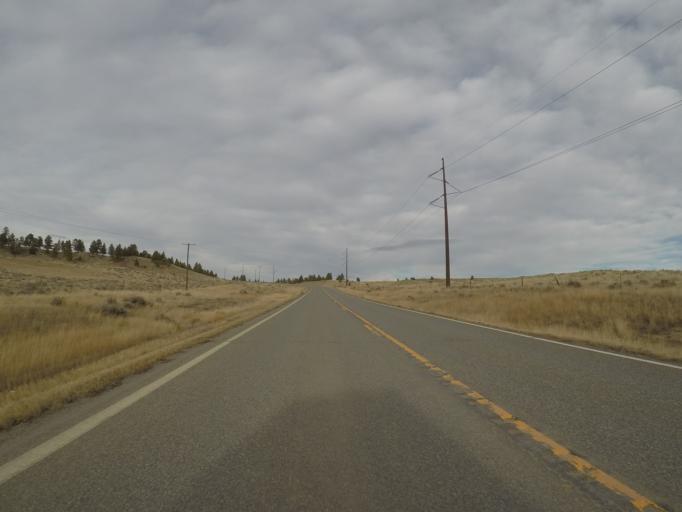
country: US
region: Montana
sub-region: Yellowstone County
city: Laurel
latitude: 45.8360
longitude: -108.7220
